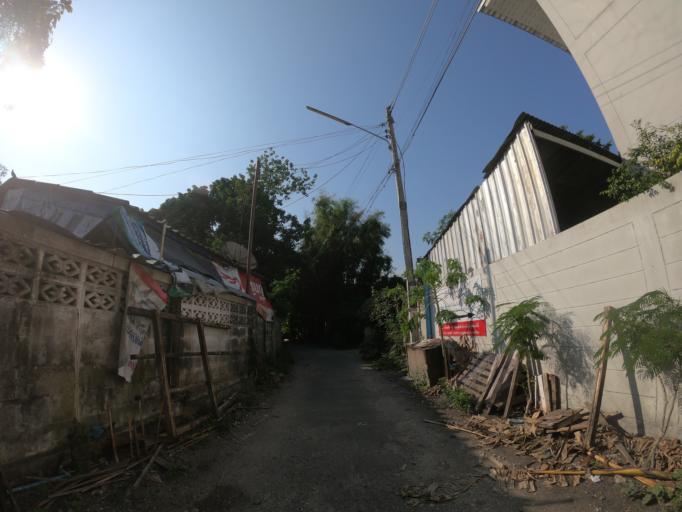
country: TH
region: Chiang Mai
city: Chiang Mai
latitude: 18.8044
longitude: 99.0139
